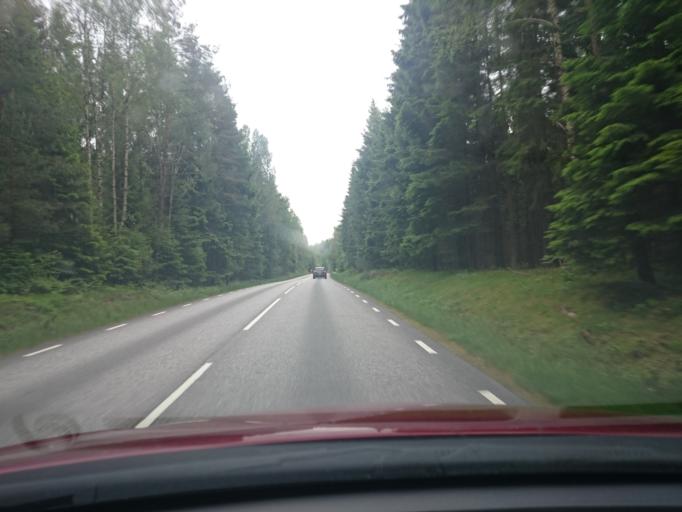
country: SE
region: Vaestra Goetaland
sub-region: Lerums Kommun
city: Stenkullen
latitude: 57.7632
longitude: 12.3075
